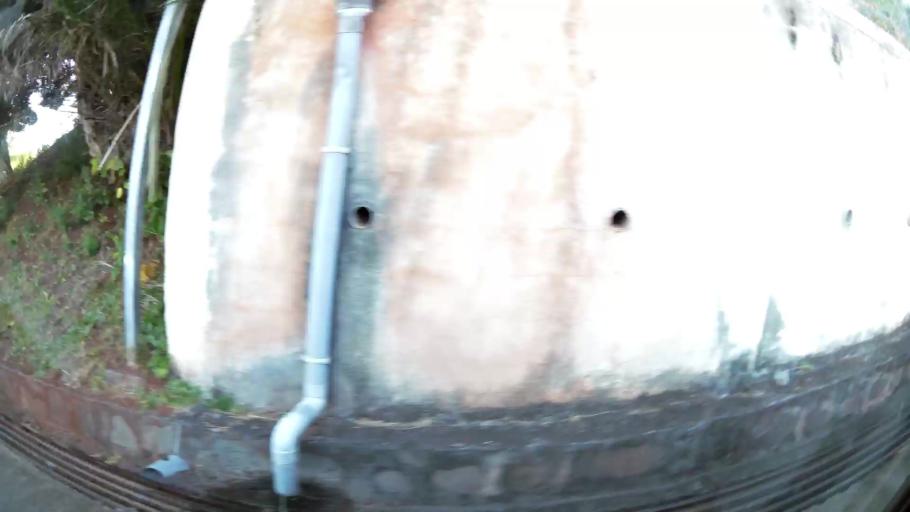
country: YT
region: Koungou
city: Koungou
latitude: -12.7441
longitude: 45.2170
